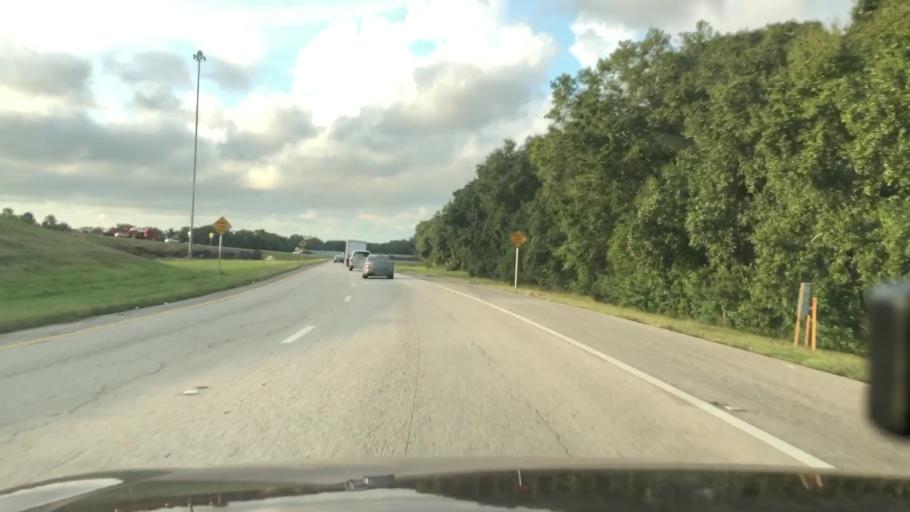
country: US
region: Florida
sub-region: Sarasota County
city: Desoto Lakes
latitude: 27.4422
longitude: -82.4573
